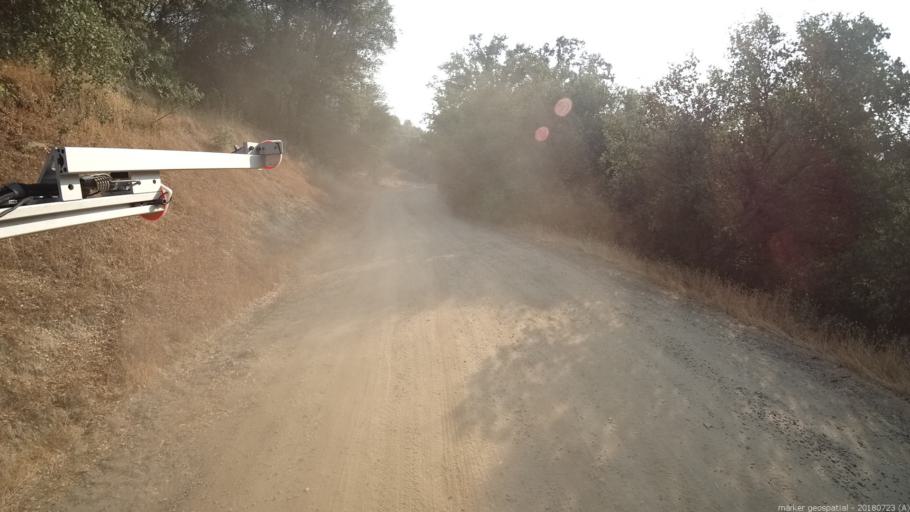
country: US
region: California
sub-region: Madera County
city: Ahwahnee
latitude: 37.3617
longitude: -119.7349
